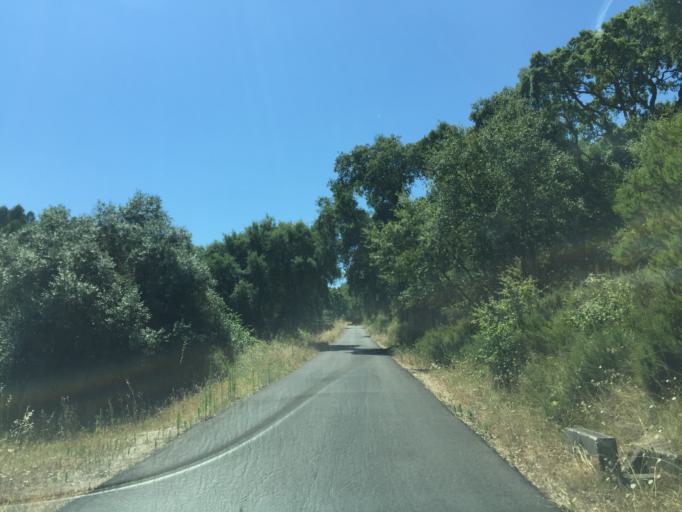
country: PT
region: Santarem
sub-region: Ferreira do Zezere
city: Ferreira do Zezere
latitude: 39.5979
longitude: -8.2716
